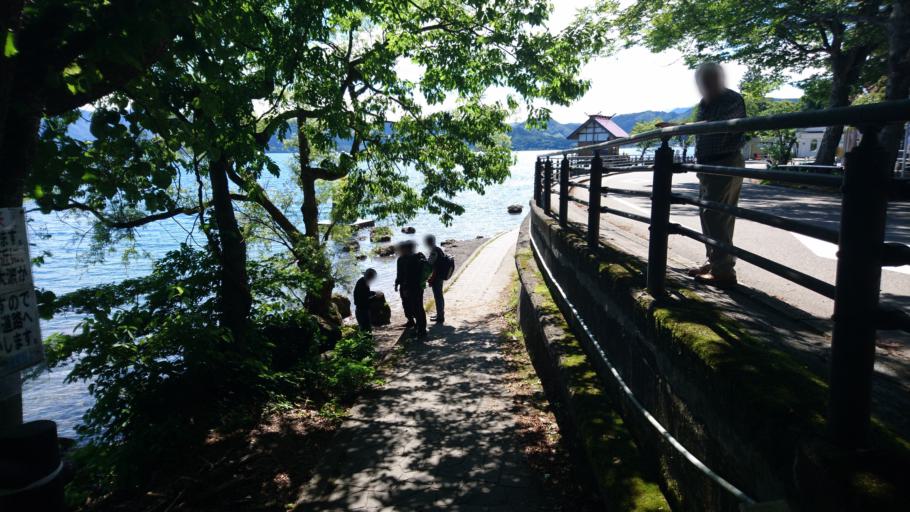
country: JP
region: Akita
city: Kakunodatemachi
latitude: 39.7140
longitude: 140.6340
